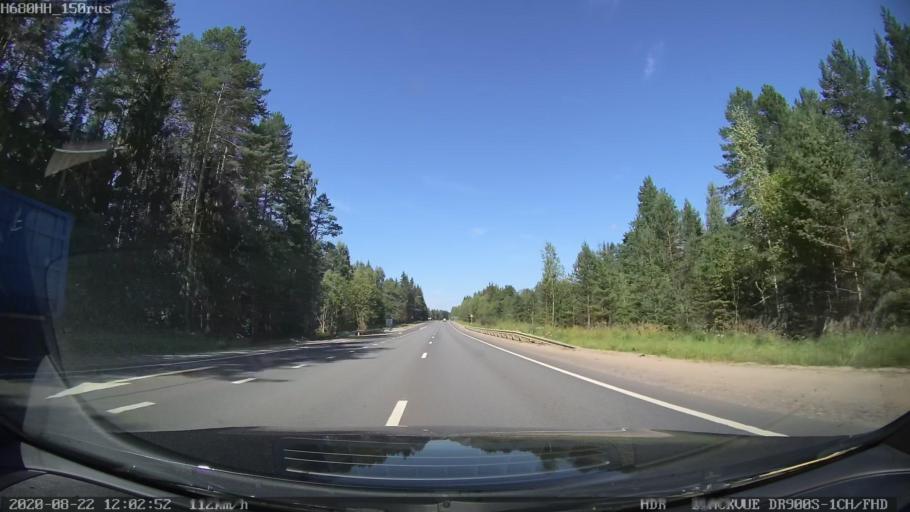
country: RU
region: Tverskaya
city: Rameshki
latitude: 57.2476
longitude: 36.0938
